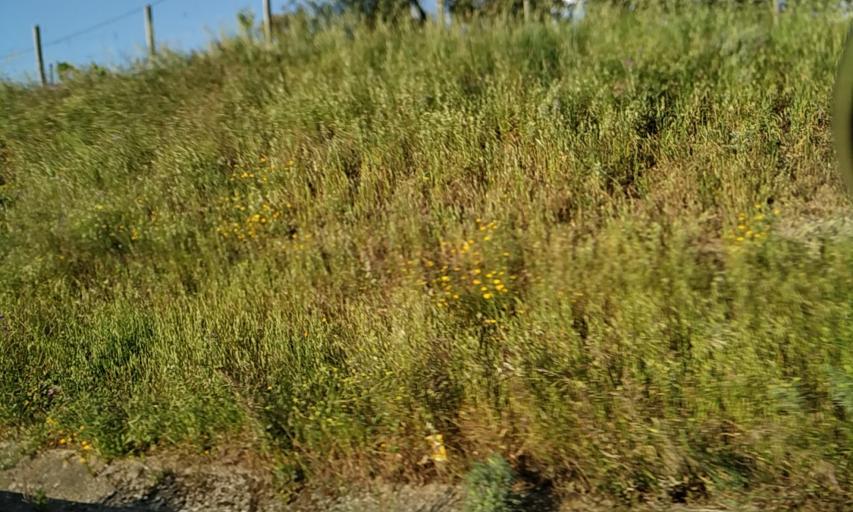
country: PT
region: Portalegre
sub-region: Portalegre
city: Portalegre
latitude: 39.3044
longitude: -7.4406
